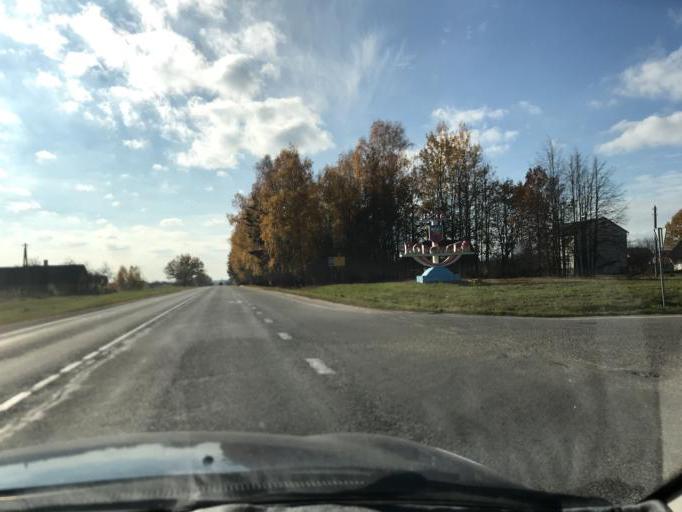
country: BY
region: Grodnenskaya
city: Voranava
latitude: 54.1666
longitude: 25.3301
